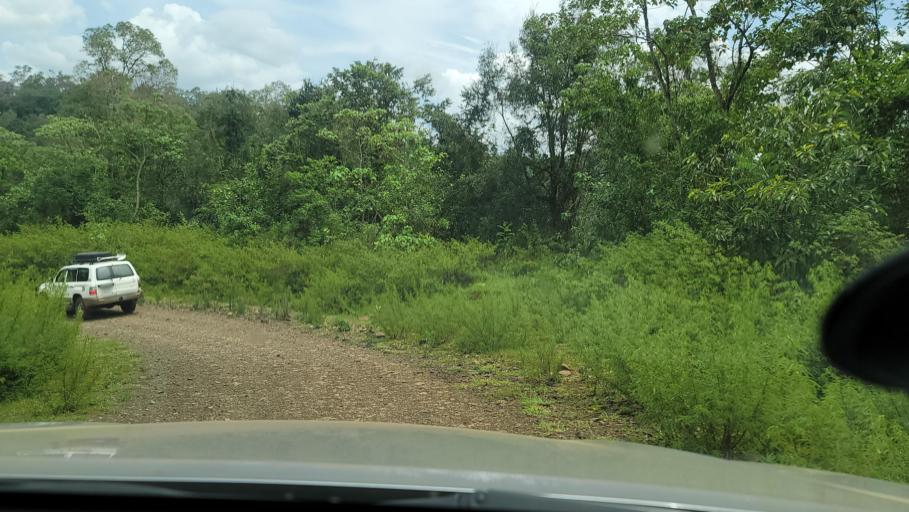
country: ET
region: Southern Nations, Nationalities, and People's Region
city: Bonga
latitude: 7.6376
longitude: 36.2298
